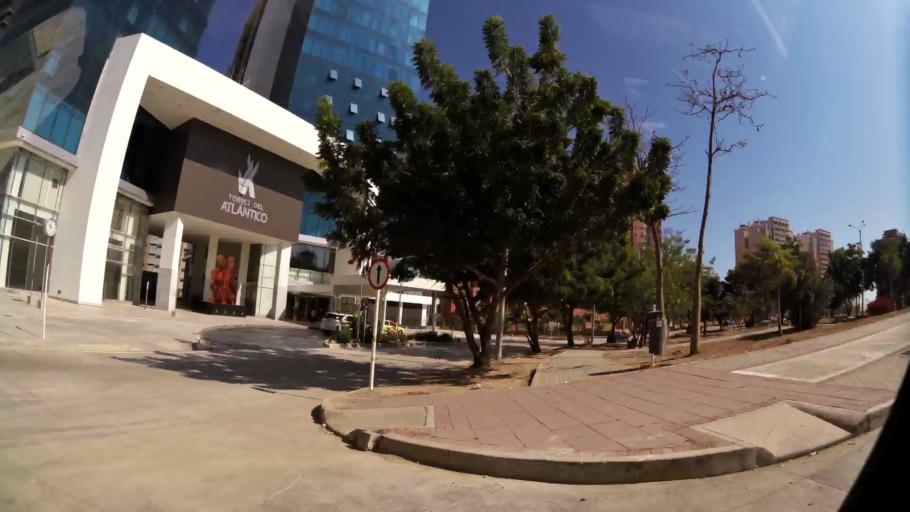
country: CO
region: Atlantico
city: Barranquilla
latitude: 11.0158
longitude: -74.8277
